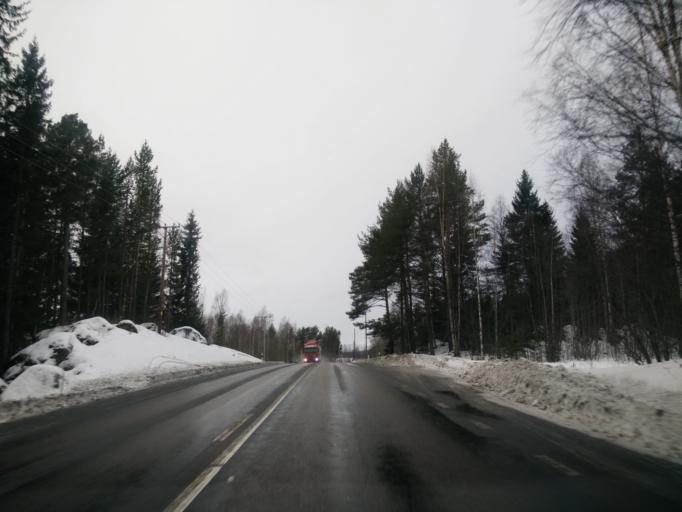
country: SE
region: Vaesternorrland
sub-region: Sundsvalls Kommun
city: Matfors
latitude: 62.4108
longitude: 16.6535
